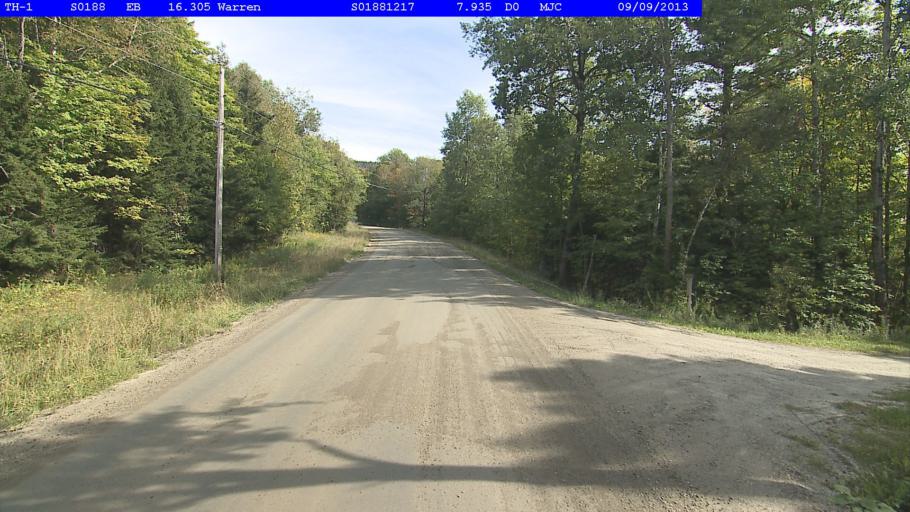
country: US
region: Vermont
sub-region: Washington County
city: Northfield
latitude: 44.1071
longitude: -72.7984
